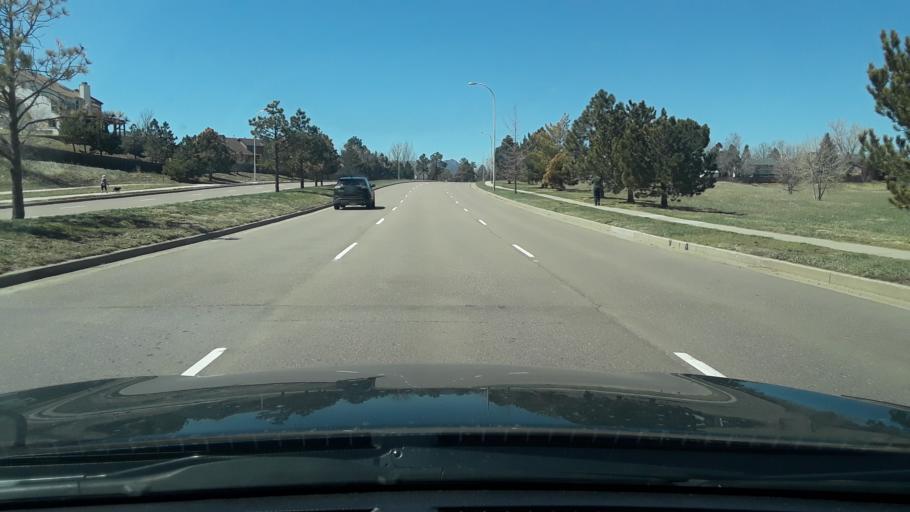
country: US
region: Colorado
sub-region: El Paso County
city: Black Forest
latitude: 38.9547
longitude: -104.7419
